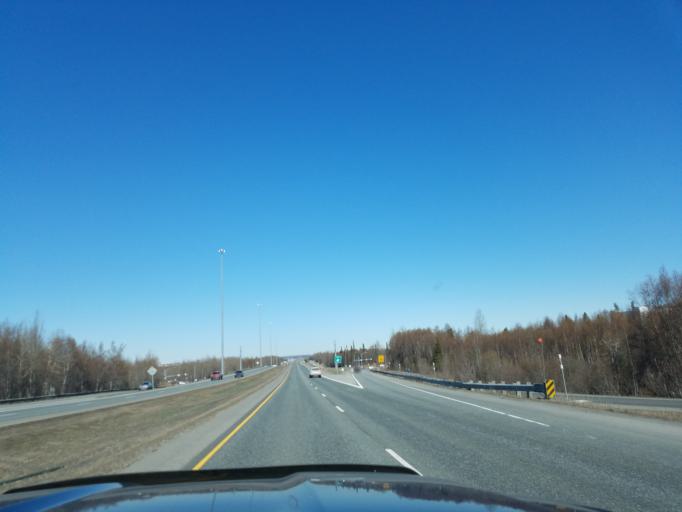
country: US
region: Alaska
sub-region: Anchorage Municipality
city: Anchorage
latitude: 61.1196
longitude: -149.8563
